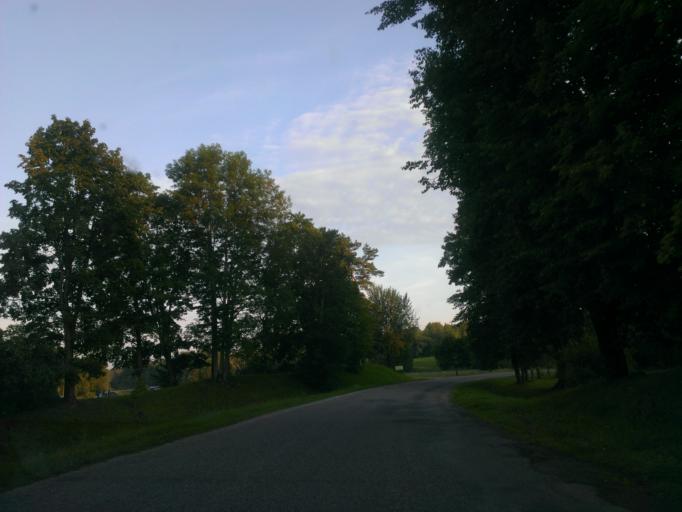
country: LV
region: Amatas Novads
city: Drabesi
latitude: 57.2508
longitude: 25.2794
